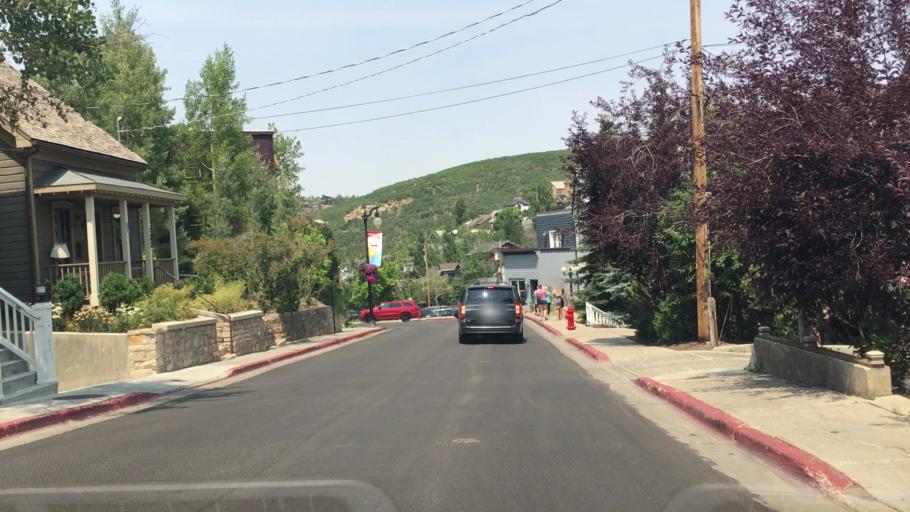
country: US
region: Utah
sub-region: Summit County
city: Park City
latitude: 40.6402
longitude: -111.4943
